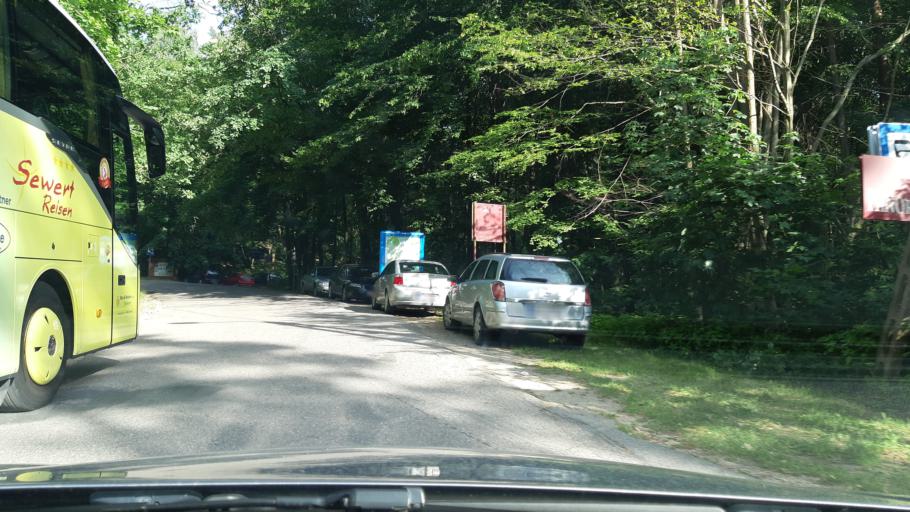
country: PL
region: Warmian-Masurian Voivodeship
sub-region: Powiat mragowski
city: Mragowo
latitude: 53.8732
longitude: 21.3223
